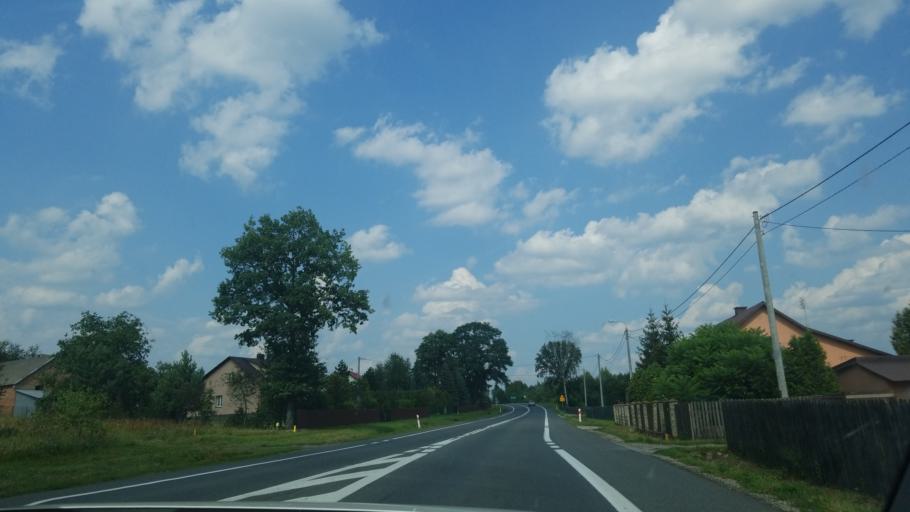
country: PL
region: Subcarpathian Voivodeship
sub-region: Powiat nizanski
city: Zarzecze
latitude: 50.5386
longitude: 22.2215
